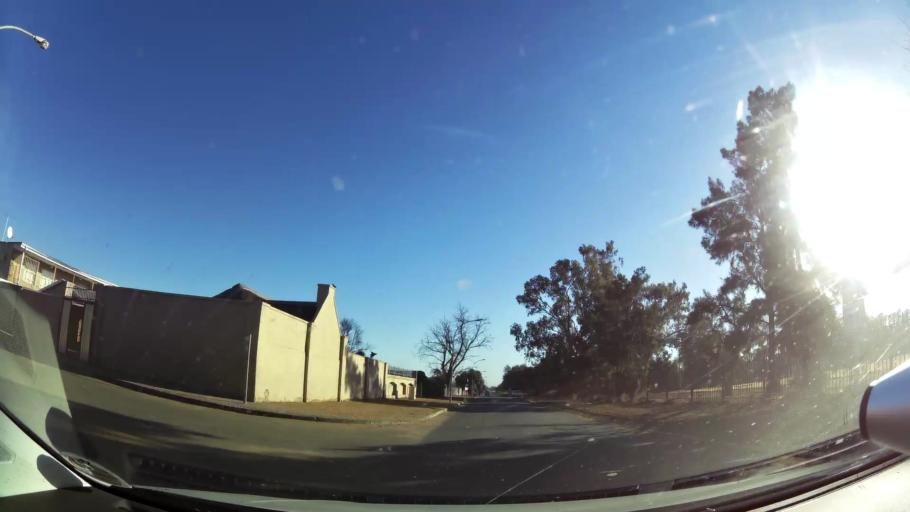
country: ZA
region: Northern Cape
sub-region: Frances Baard District Municipality
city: Kimberley
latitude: -28.7369
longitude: 24.7353
